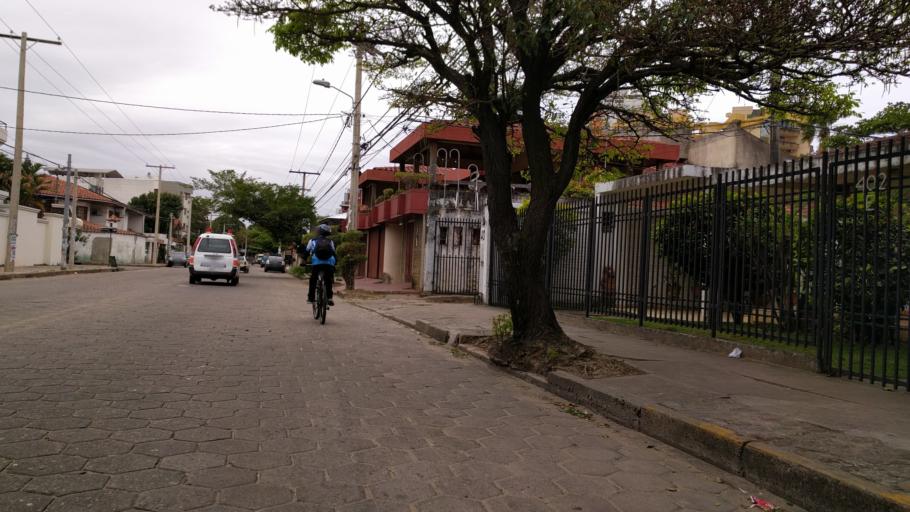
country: BO
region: Santa Cruz
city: Santa Cruz de la Sierra
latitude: -17.7757
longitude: -63.1690
